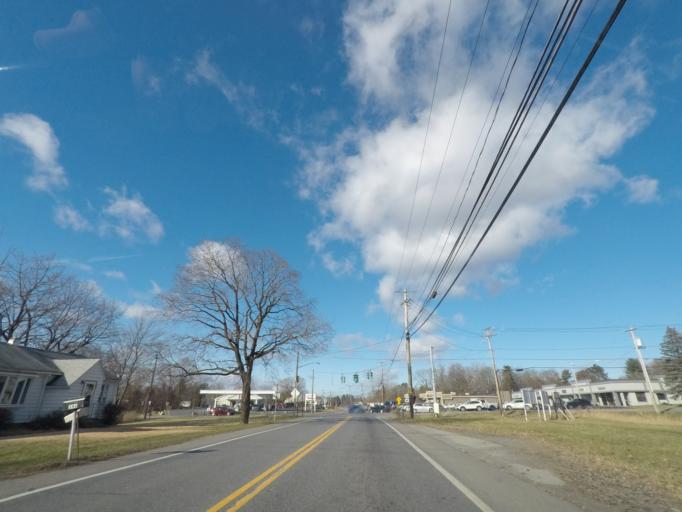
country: US
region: New York
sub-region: Saratoga County
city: Waterford
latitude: 42.8372
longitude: -73.7377
